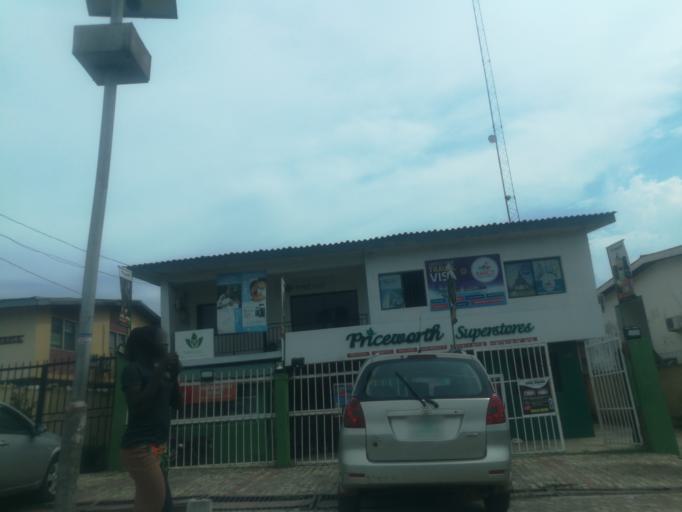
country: NG
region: Oyo
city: Ibadan
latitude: 7.4230
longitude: 3.9121
